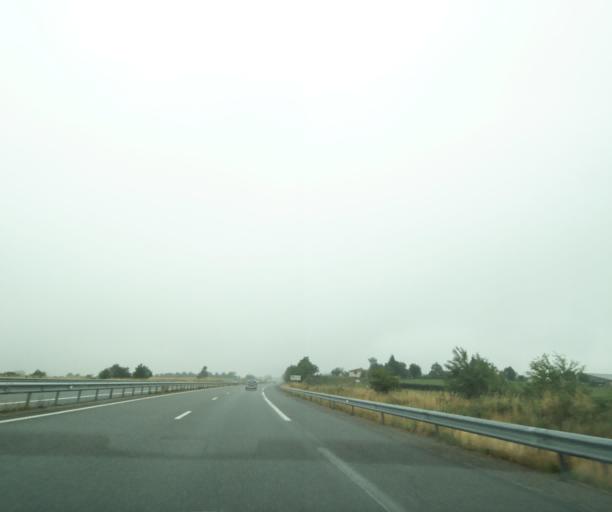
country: FR
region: Midi-Pyrenees
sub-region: Departement de l'Aveyron
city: Naucelle
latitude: 44.1313
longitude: 2.3084
